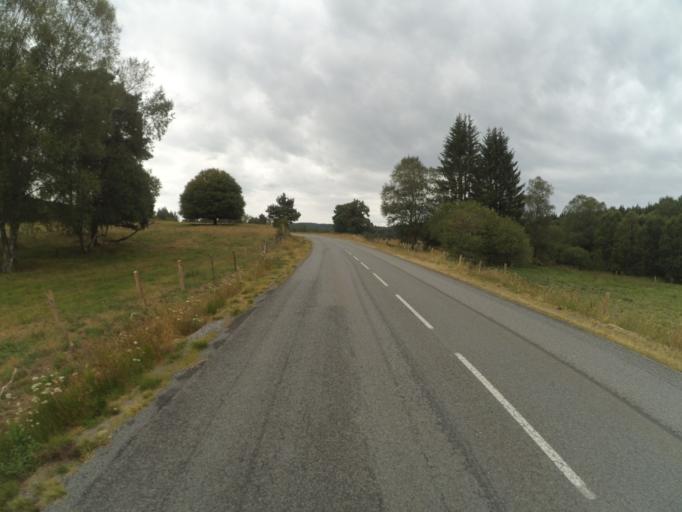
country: FR
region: Limousin
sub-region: Departement de la Correze
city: Meymac
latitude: 45.6903
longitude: 2.0788
